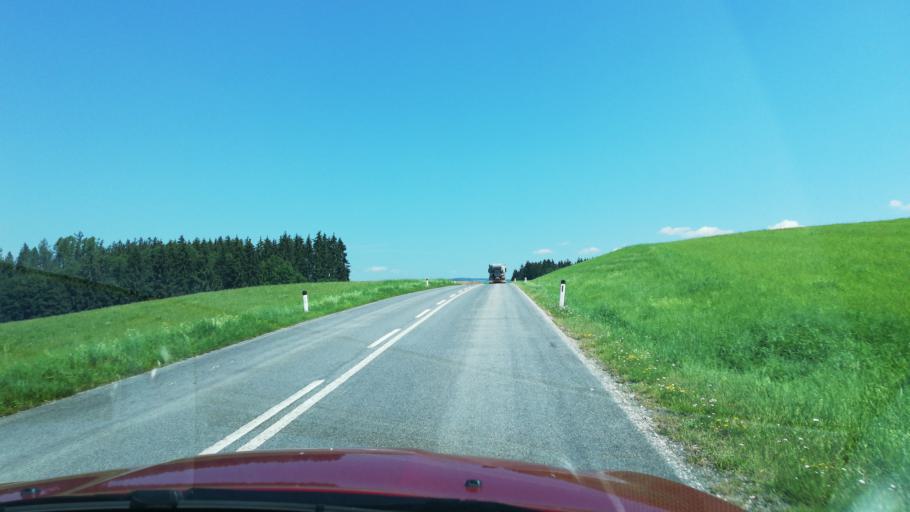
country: AT
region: Upper Austria
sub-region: Politischer Bezirk Urfahr-Umgebung
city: Herzogsdorf
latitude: 48.4670
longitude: 14.0593
